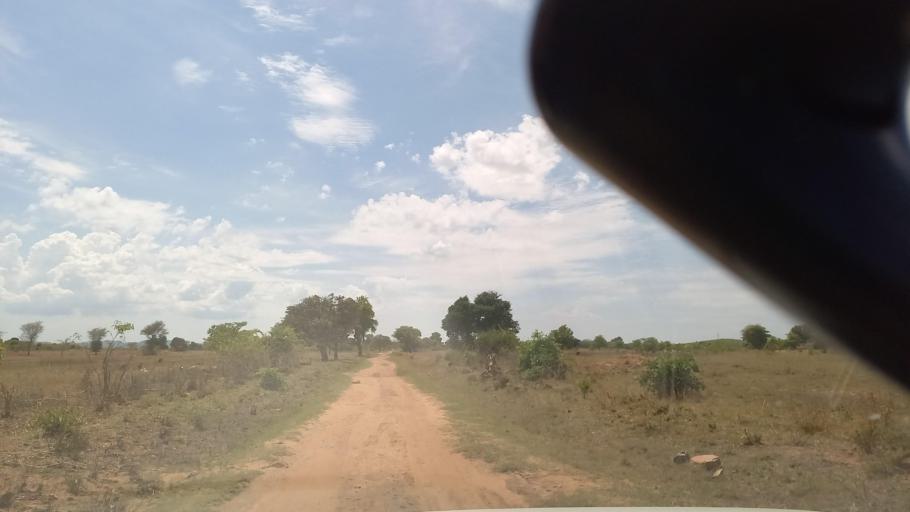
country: ZM
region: Southern
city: Mazabuka
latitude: -16.1448
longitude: 27.7719
